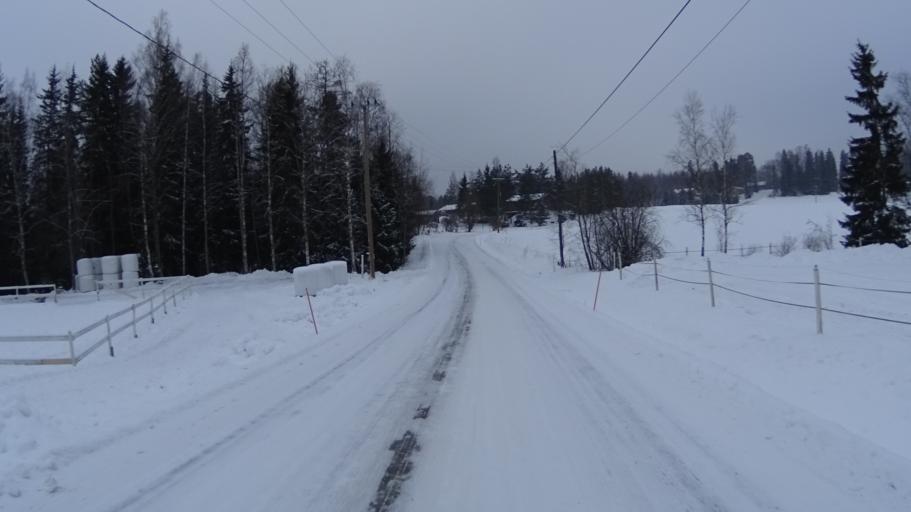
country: FI
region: Uusimaa
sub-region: Helsinki
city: Vihti
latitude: 60.3494
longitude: 24.2127
